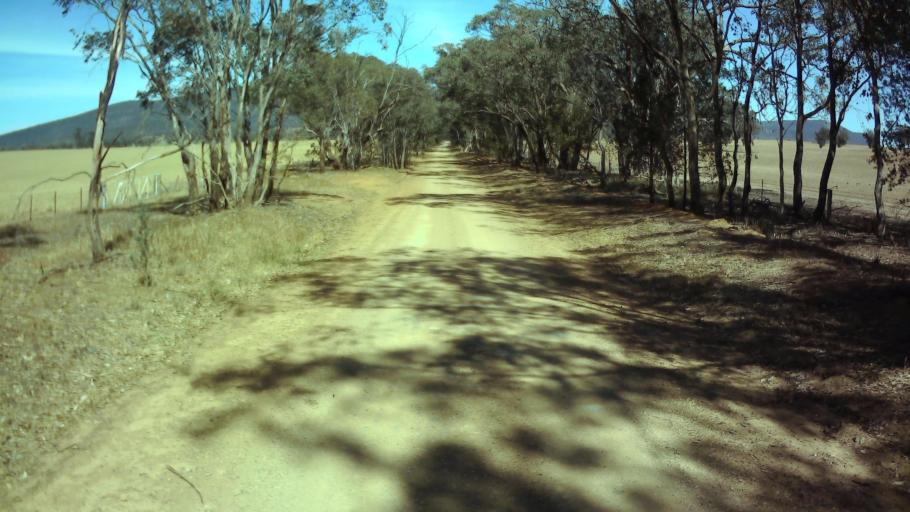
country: AU
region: New South Wales
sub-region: Weddin
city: Grenfell
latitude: -33.9406
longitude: 148.0610
